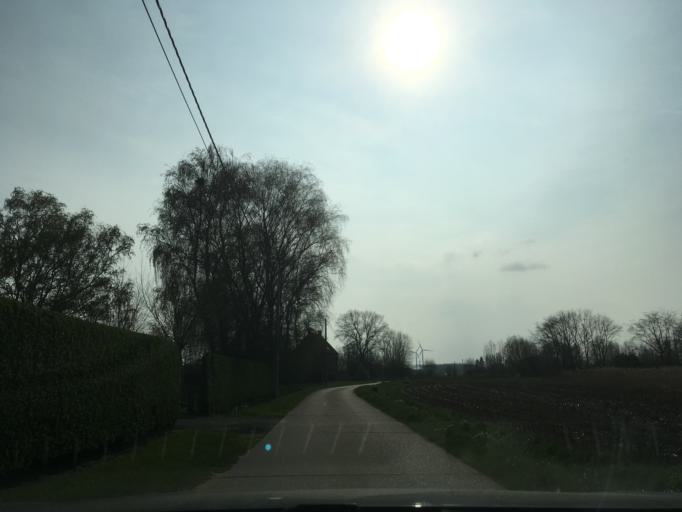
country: BE
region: Flanders
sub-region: Provincie West-Vlaanderen
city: Ardooie
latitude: 50.9562
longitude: 3.1962
